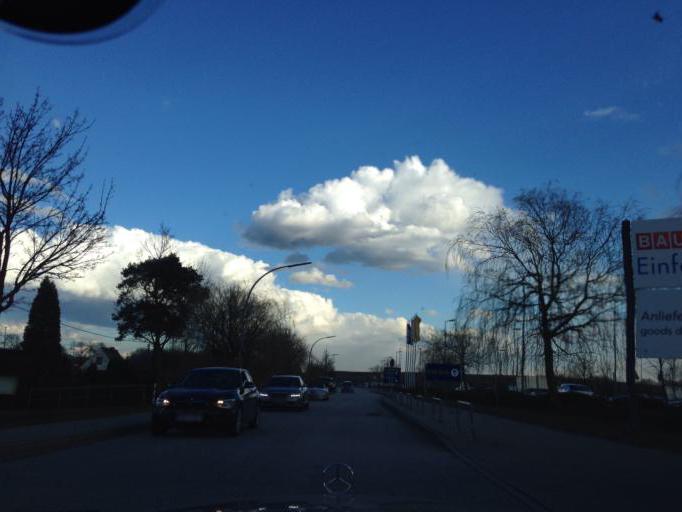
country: DE
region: Hamburg
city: Wandsbek
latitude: 53.5128
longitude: 10.0943
